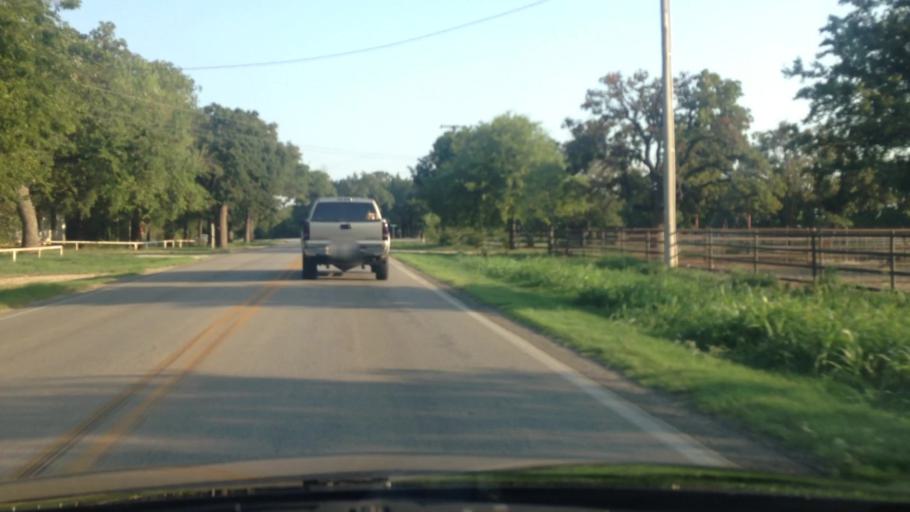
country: US
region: Texas
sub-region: Tarrant County
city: Everman
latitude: 32.6079
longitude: -97.2672
